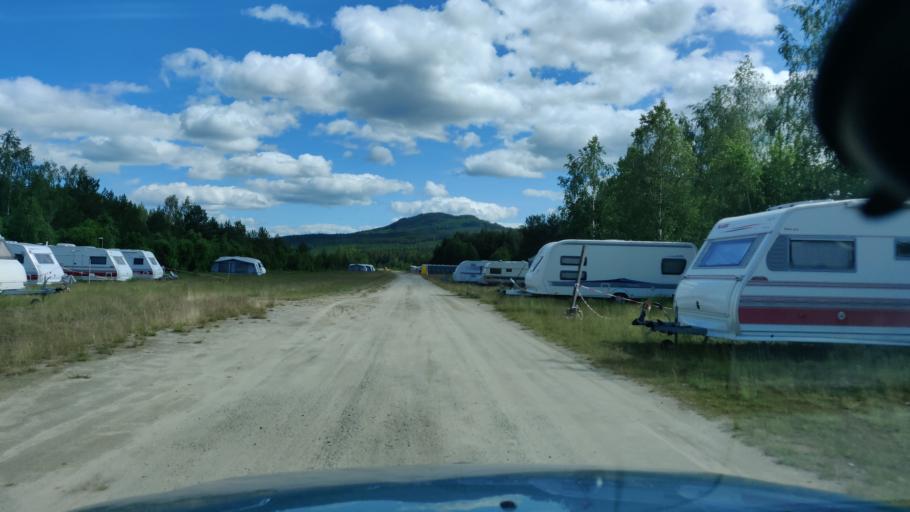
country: NO
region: Hedmark
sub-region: Trysil
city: Innbygda
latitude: 60.9099
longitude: 12.5653
